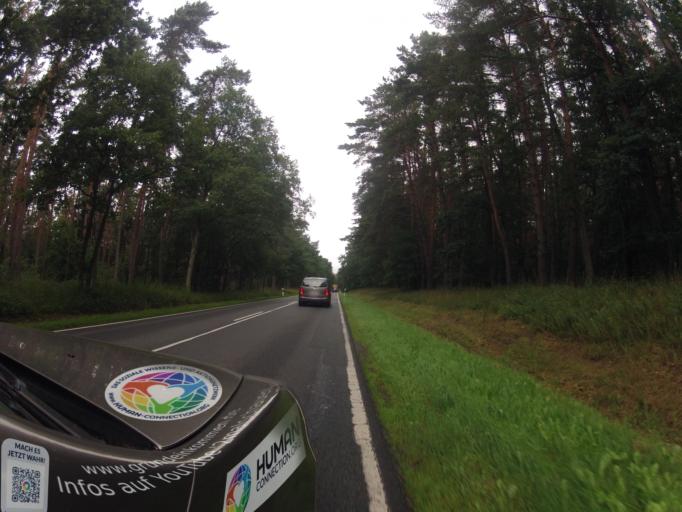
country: DE
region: Mecklenburg-Vorpommern
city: Lassan
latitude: 53.8918
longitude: 13.7885
